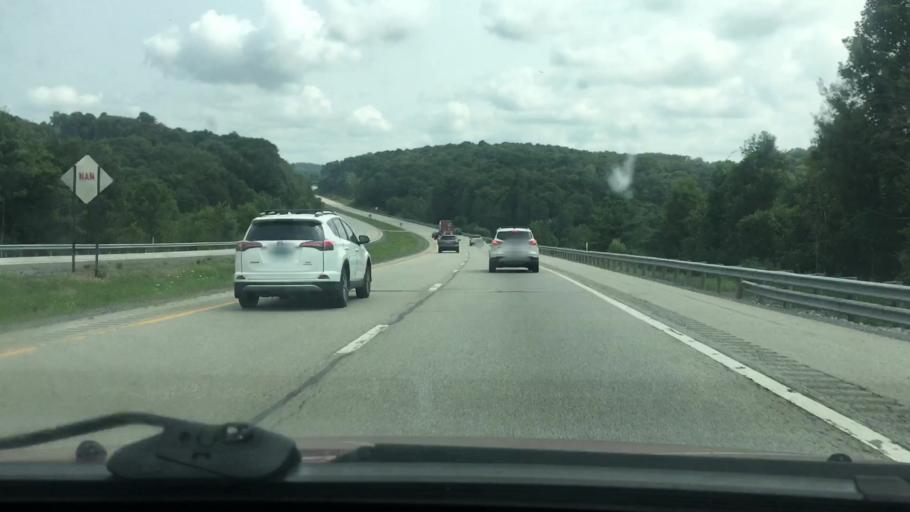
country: US
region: West Virginia
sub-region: Monongalia County
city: Cheat Lake
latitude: 39.6567
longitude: -79.6860
